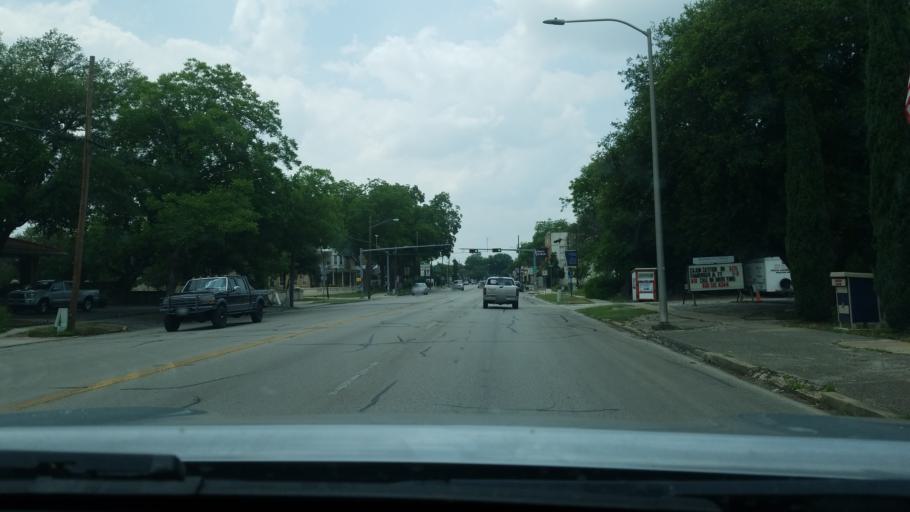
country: US
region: Texas
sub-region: Comal County
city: New Braunfels
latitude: 29.7008
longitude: -98.1212
